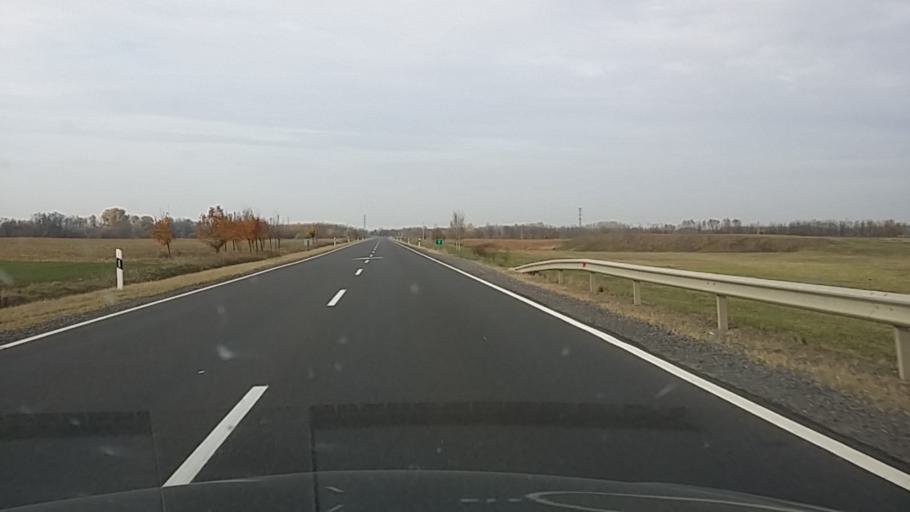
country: HU
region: Szabolcs-Szatmar-Bereg
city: Nyirpazony
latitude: 47.9549
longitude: 21.8196
